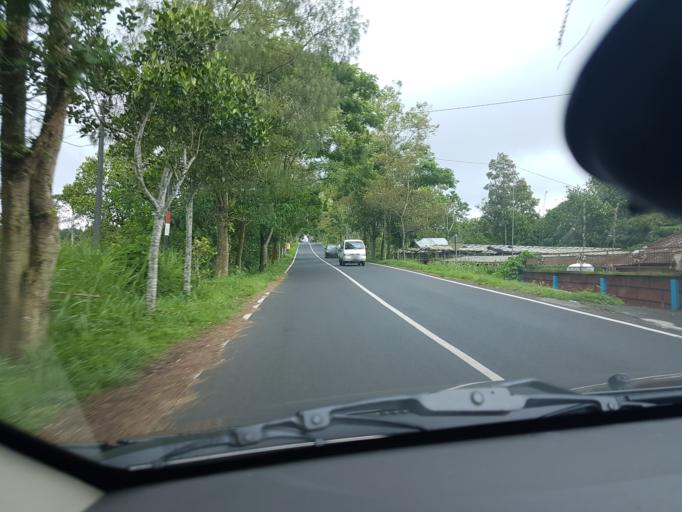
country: ID
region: Bali
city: Banjar Kedisan
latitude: -8.2909
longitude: 115.3601
